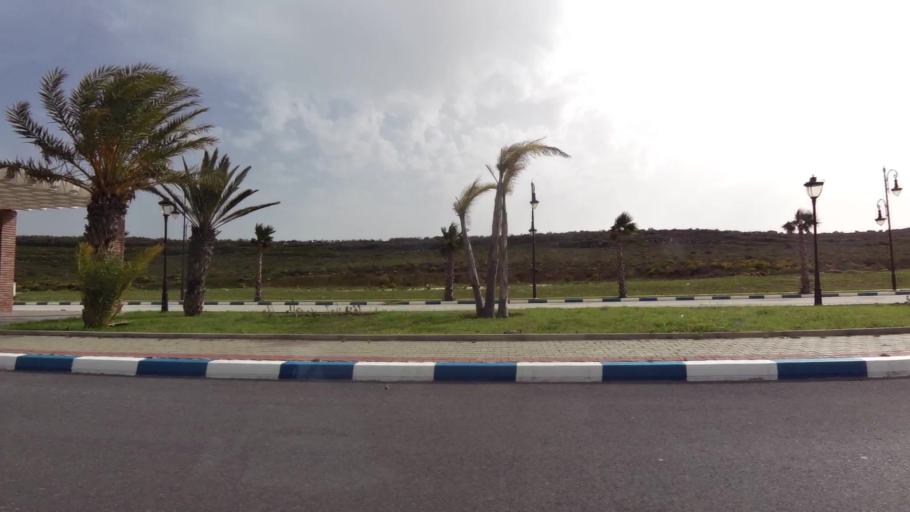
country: MA
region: Tanger-Tetouan
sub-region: Tanger-Assilah
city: Boukhalef
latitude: 35.6983
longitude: -5.9296
